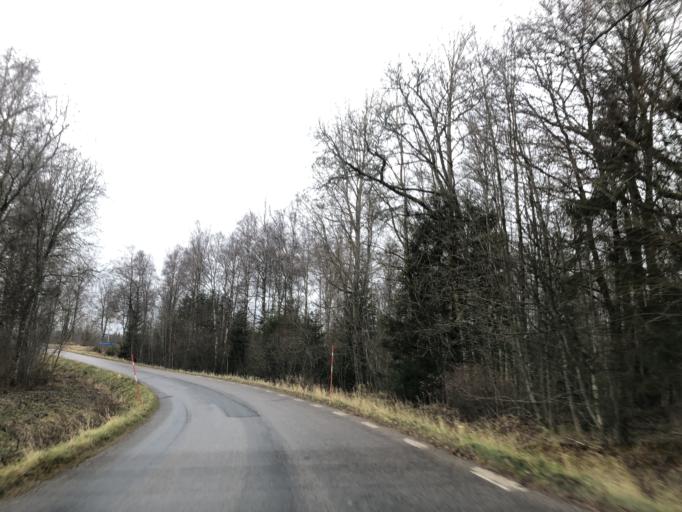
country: SE
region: Vaestra Goetaland
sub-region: Ulricehamns Kommun
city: Ulricehamn
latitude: 57.8928
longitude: 13.5100
